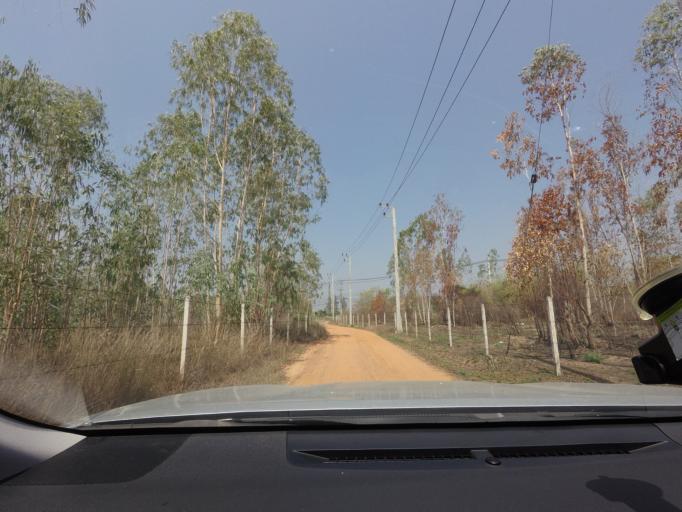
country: TH
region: Prachuap Khiri Khan
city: Prachuap Khiri Khan
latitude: 11.9337
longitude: 99.8159
